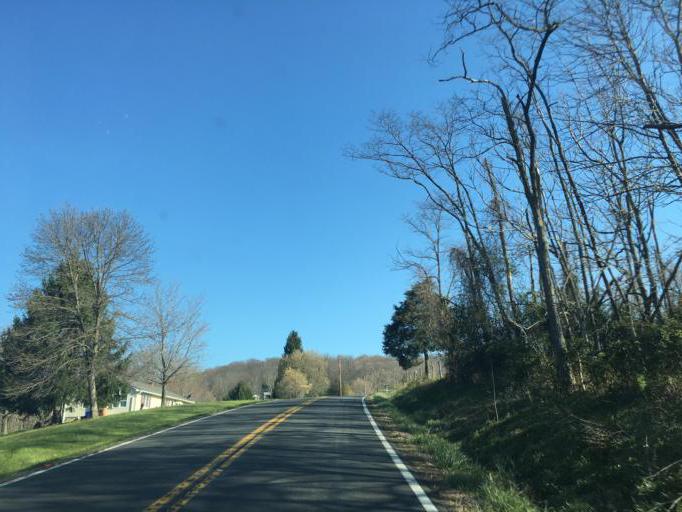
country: US
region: Maryland
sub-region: Frederick County
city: Myersville
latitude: 39.5438
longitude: -77.5468
